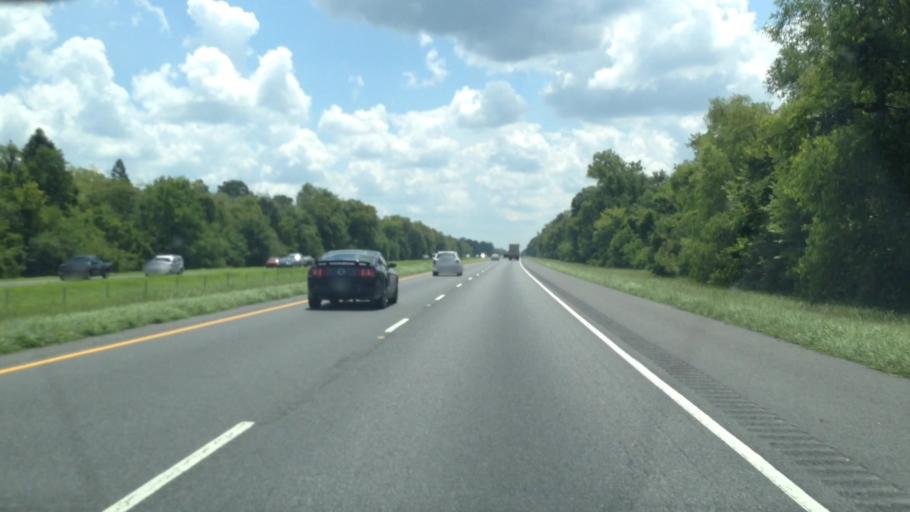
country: US
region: Louisiana
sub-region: Saint James Parish
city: Grand Point
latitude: 30.1477
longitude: -90.7733
